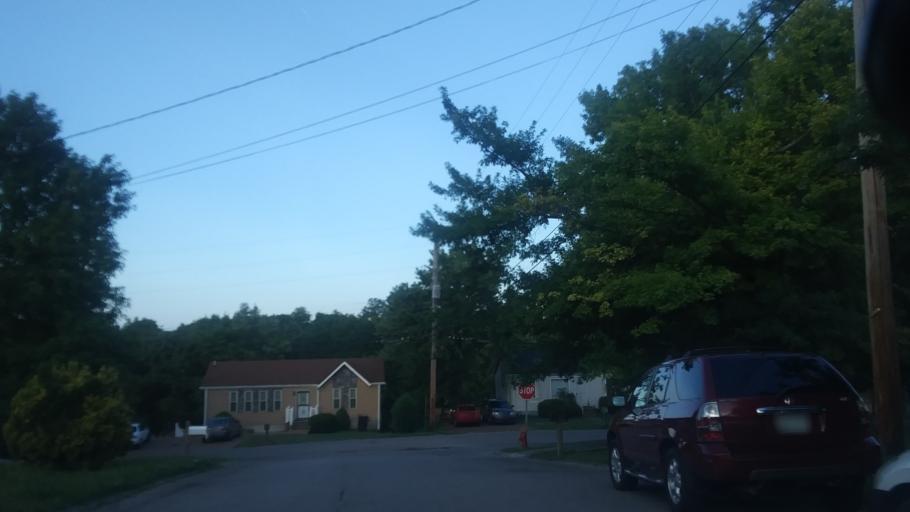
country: US
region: Tennessee
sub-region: Rutherford County
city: La Vergne
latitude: 36.0740
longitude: -86.6699
